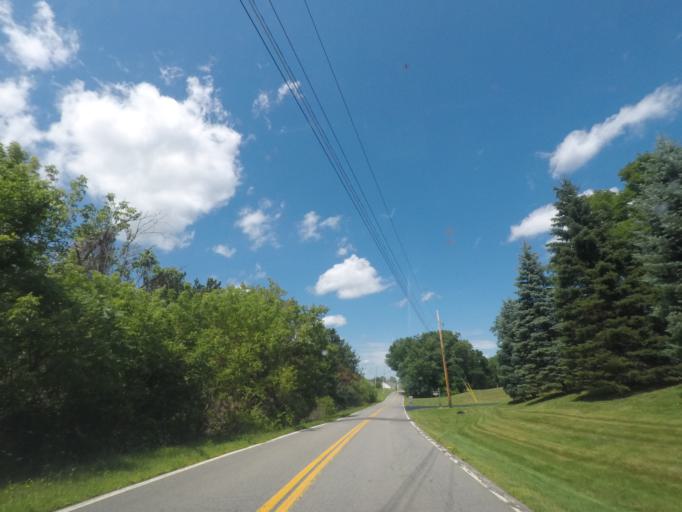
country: US
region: New York
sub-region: Schenectady County
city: Rotterdam
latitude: 42.7191
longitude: -73.9596
